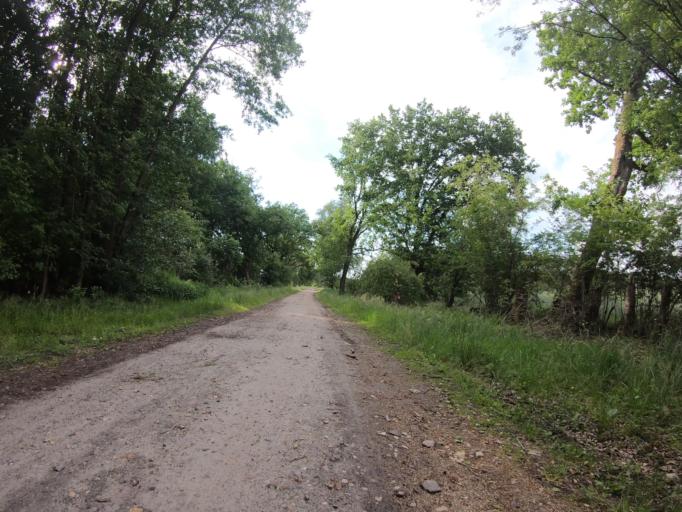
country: DE
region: Lower Saxony
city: Wesendorf
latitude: 52.5717
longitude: 10.5618
